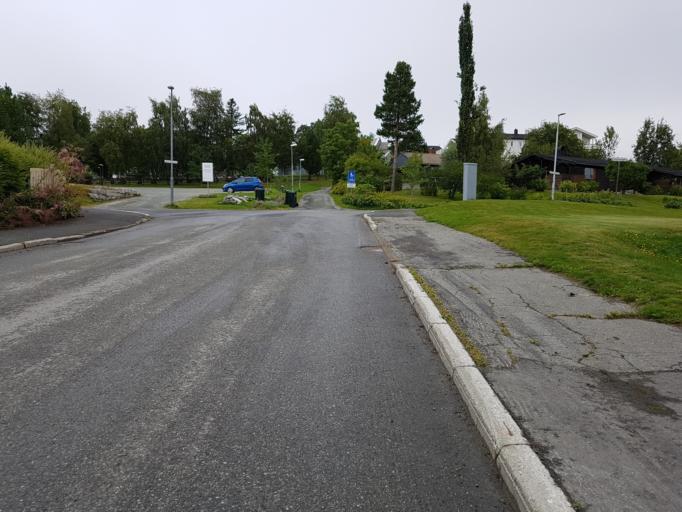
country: NO
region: Sor-Trondelag
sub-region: Trondheim
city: Trondheim
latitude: 63.4030
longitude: 10.3721
